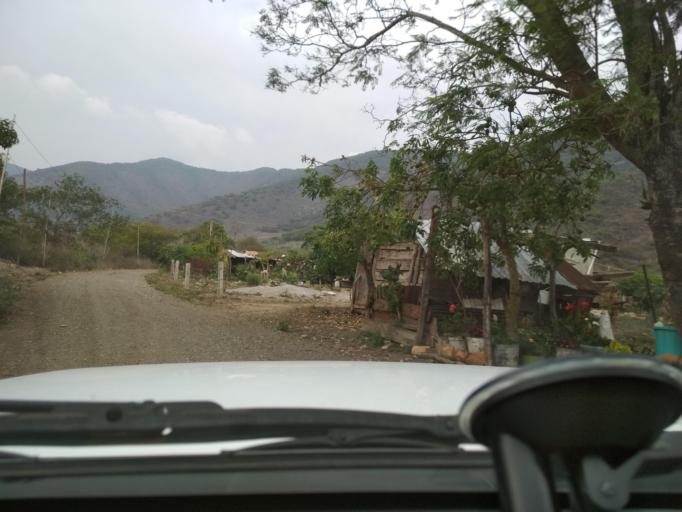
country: MX
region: Veracruz
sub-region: Nogales
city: Taza de Agua Ojo Zarco
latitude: 18.7901
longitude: -97.2155
